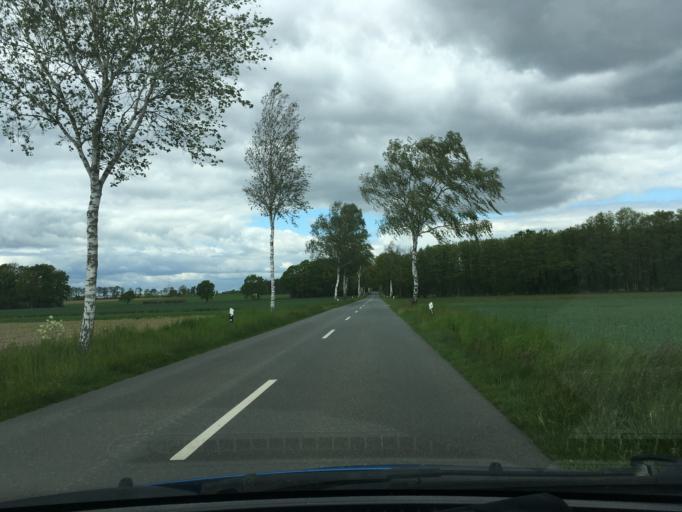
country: DE
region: Lower Saxony
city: Gerdau
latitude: 52.9300
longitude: 10.4094
